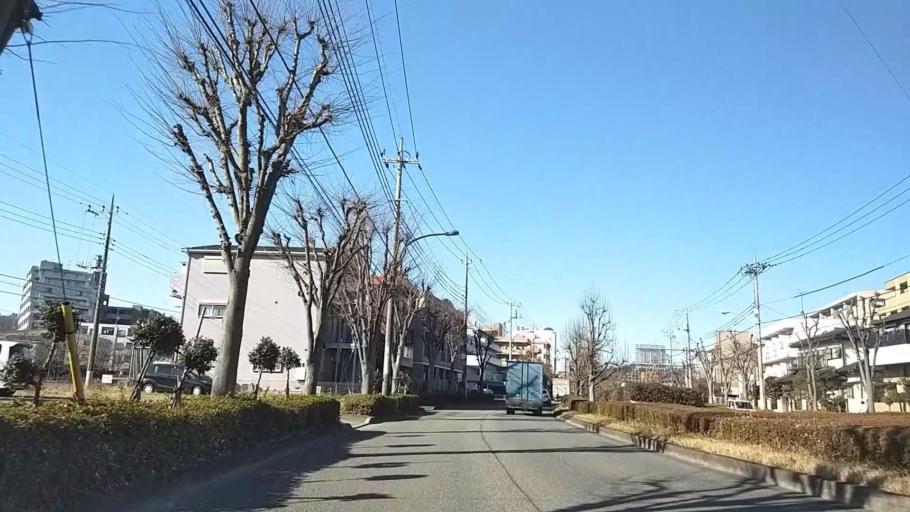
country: JP
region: Tokyo
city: Hino
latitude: 35.6273
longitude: 139.3943
